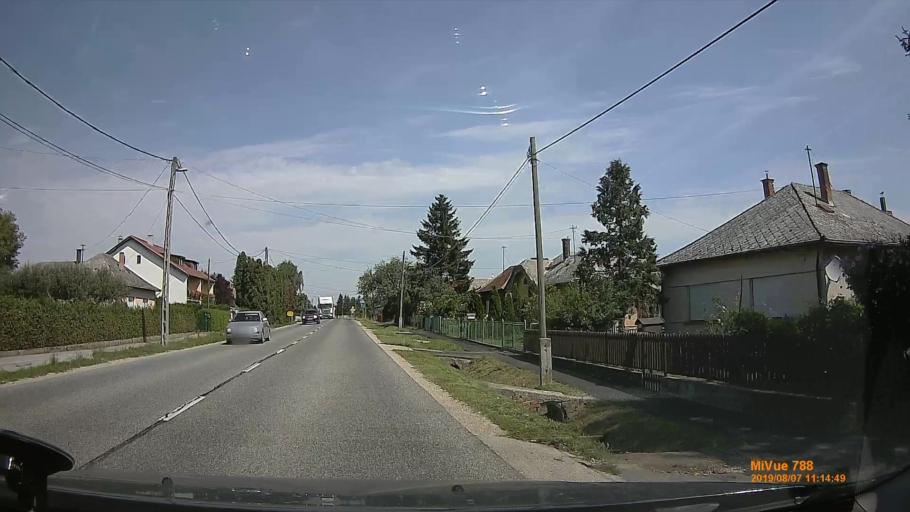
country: HU
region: Zala
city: Lenti
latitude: 46.7097
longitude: 16.5520
